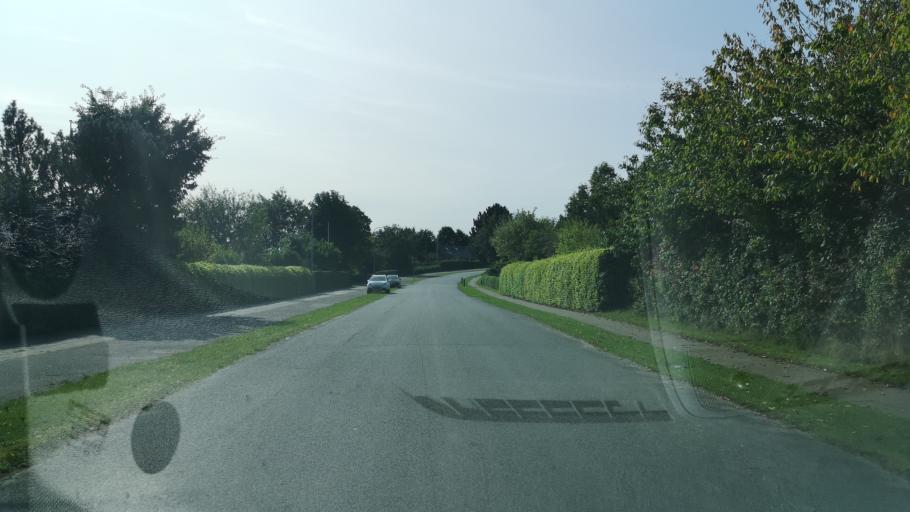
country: DK
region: Central Jutland
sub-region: Ringkobing-Skjern Kommune
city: Videbaek
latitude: 56.0837
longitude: 8.6217
